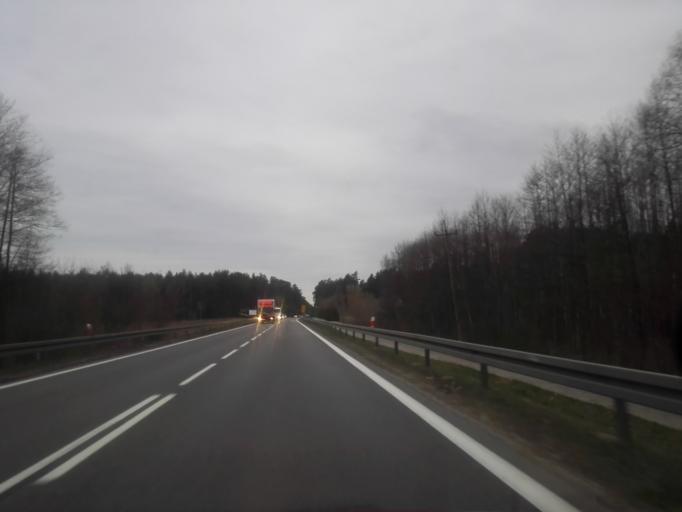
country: PL
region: Podlasie
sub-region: Powiat grajewski
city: Rajgrod
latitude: 53.7055
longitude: 22.6663
